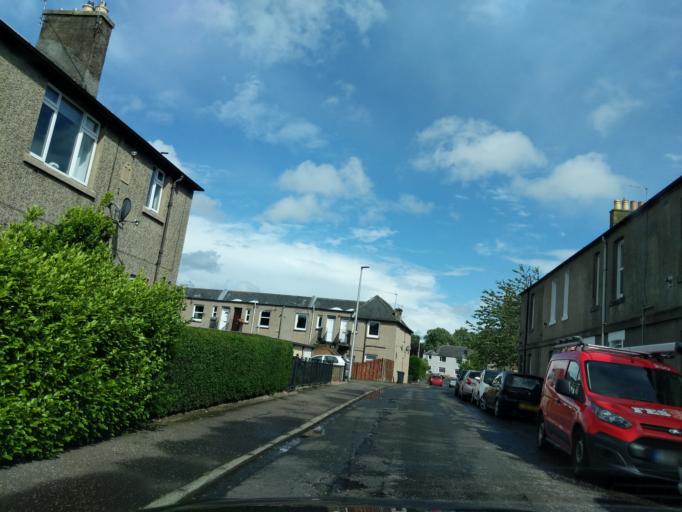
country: GB
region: Scotland
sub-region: Midlothian
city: Loanhead
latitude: 55.8595
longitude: -3.1659
